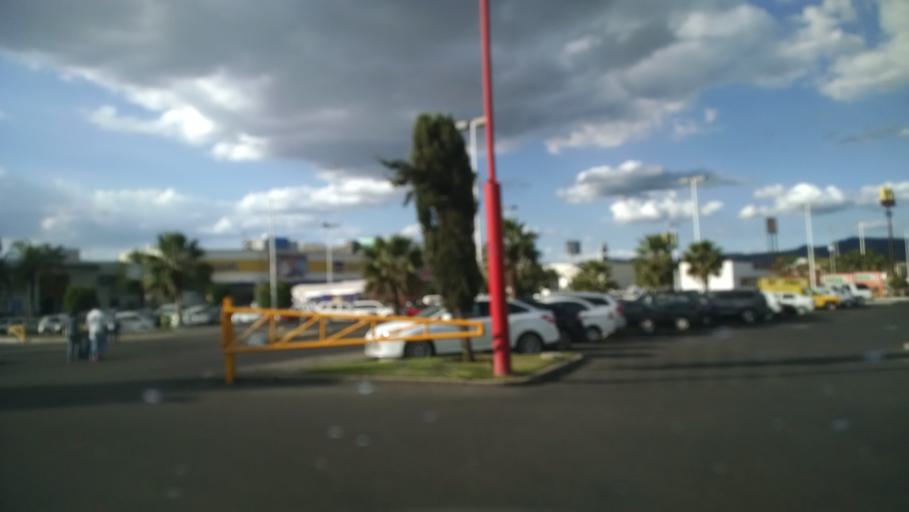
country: MX
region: Guanajuato
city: Leon
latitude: 21.0986
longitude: -101.6351
